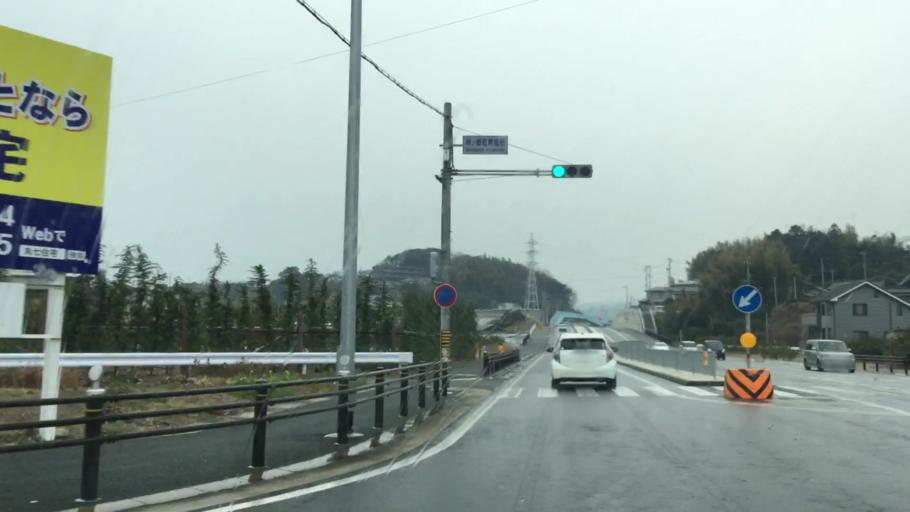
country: JP
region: Aichi
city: Gamagori
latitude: 34.8334
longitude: 137.2193
